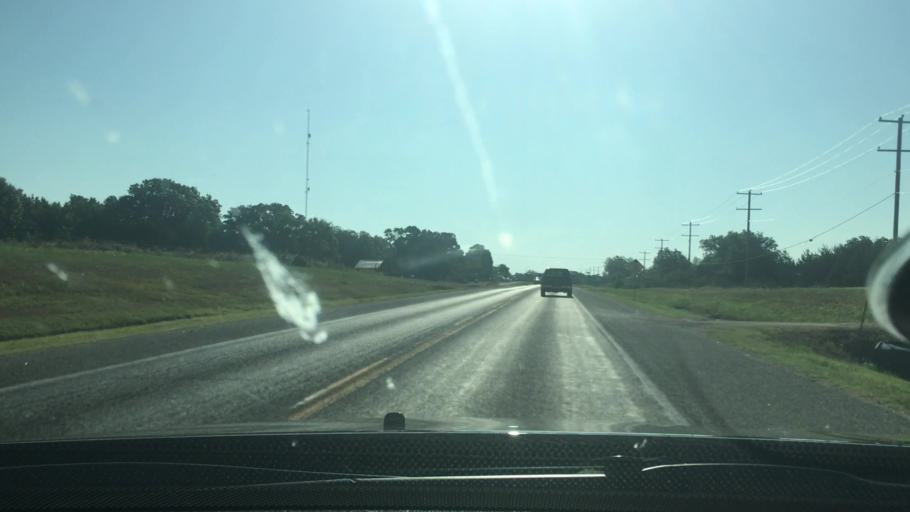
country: US
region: Oklahoma
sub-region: Johnston County
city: Tishomingo
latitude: 34.2370
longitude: -96.7078
